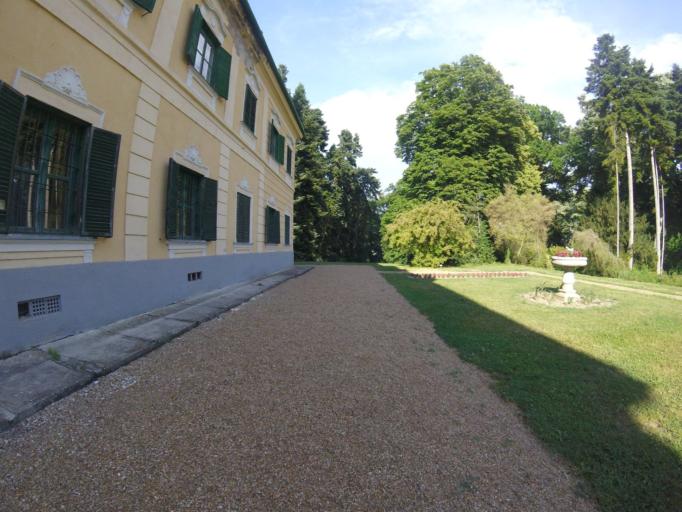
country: HU
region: Baranya
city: Sellye
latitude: 45.8705
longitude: 17.8467
